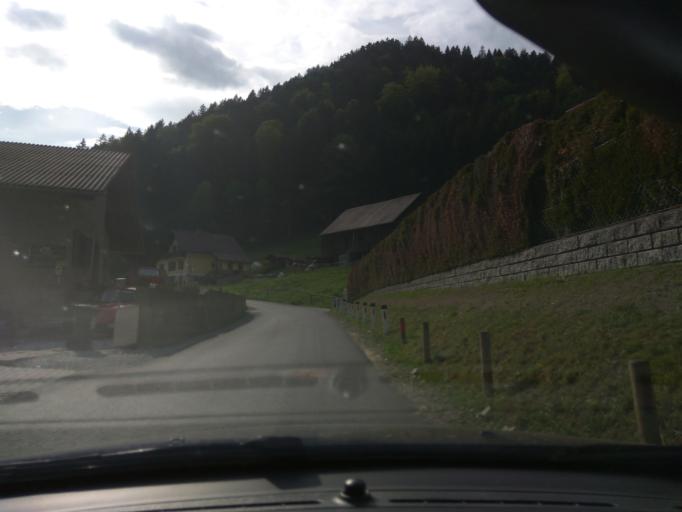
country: AT
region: Styria
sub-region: Politischer Bezirk Voitsberg
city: Voitsberg
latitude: 47.0311
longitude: 15.1266
